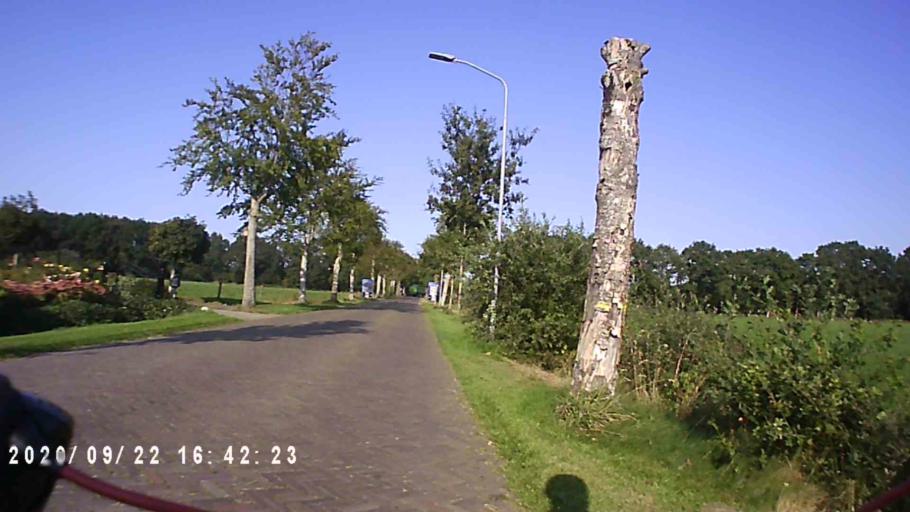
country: NL
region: Groningen
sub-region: Gemeente Leek
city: Leek
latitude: 53.1168
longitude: 6.4564
